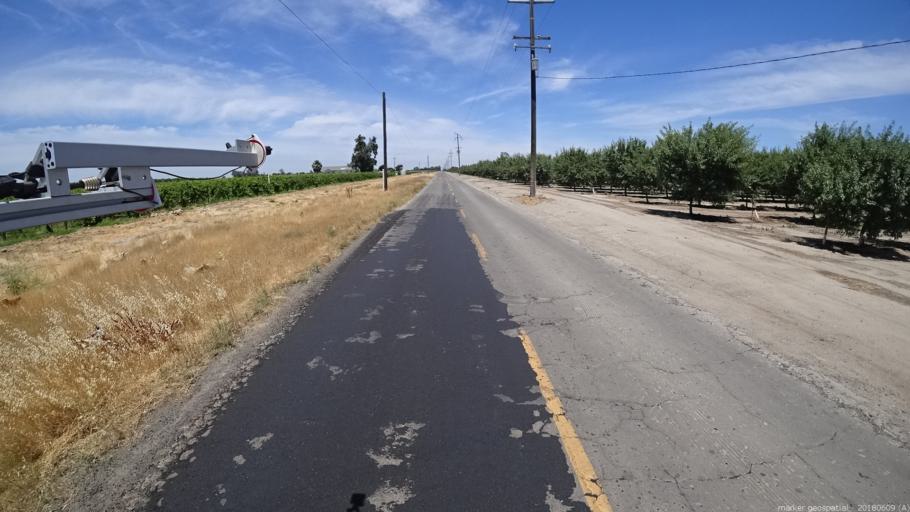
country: US
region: California
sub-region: Madera County
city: Parkwood
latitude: 36.8673
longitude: -120.1103
